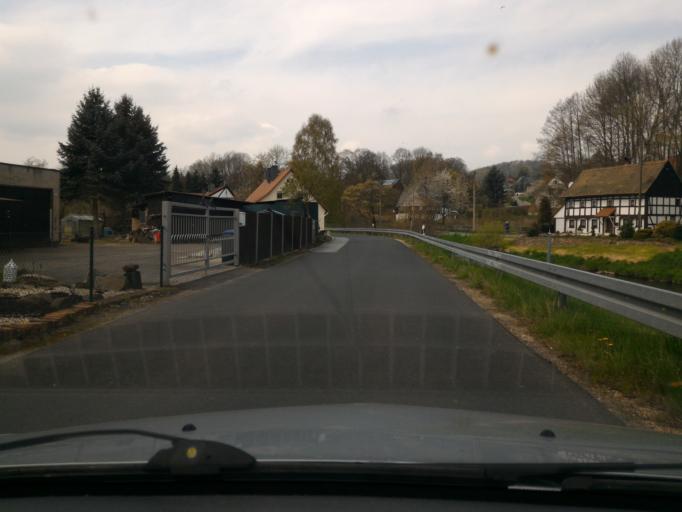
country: DE
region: Saxony
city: Hainewalde
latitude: 50.9043
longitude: 14.6993
